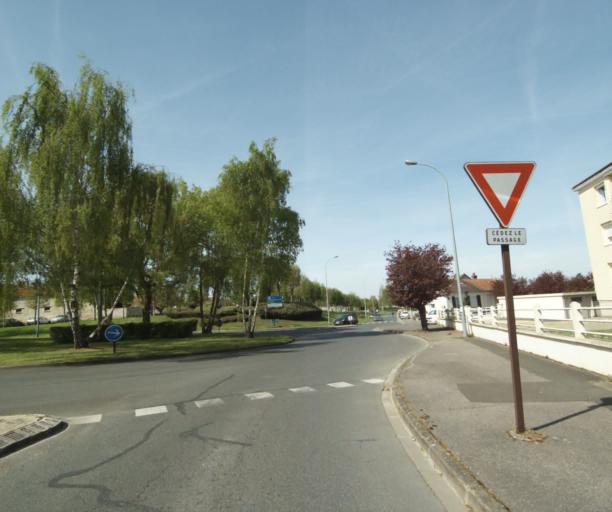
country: FR
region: Ile-de-France
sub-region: Departement de Seine-et-Marne
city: Nangis
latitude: 48.5558
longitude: 3.0198
